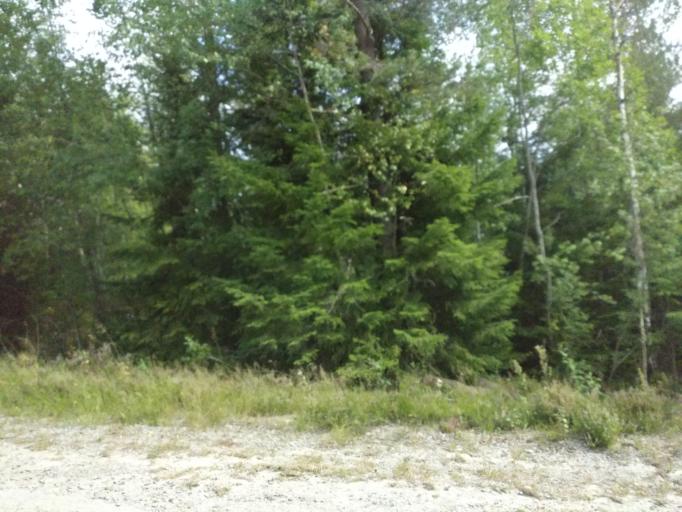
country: SE
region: Vaermland
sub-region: Hagfors Kommun
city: Hagfors
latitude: 60.0211
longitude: 13.7308
